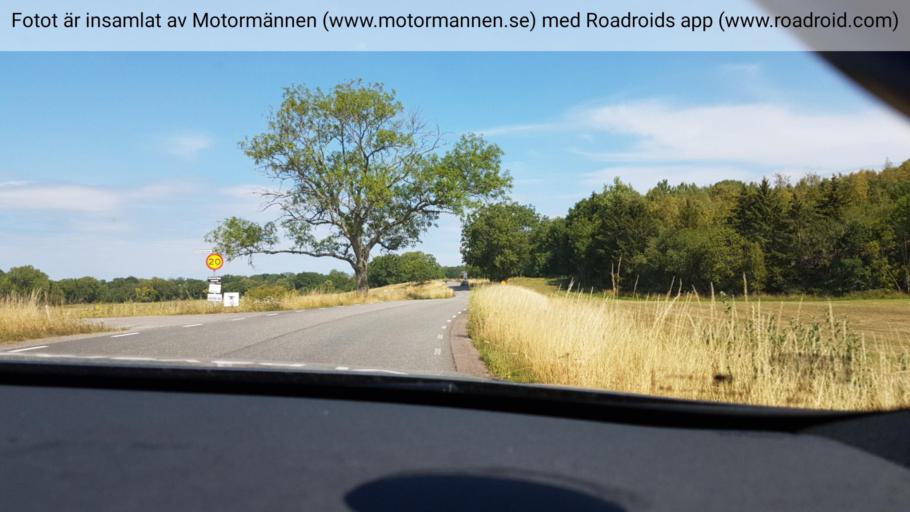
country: SE
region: Vaestra Goetaland
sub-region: Gotene Kommun
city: Kallby
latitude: 58.5373
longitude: 13.3228
